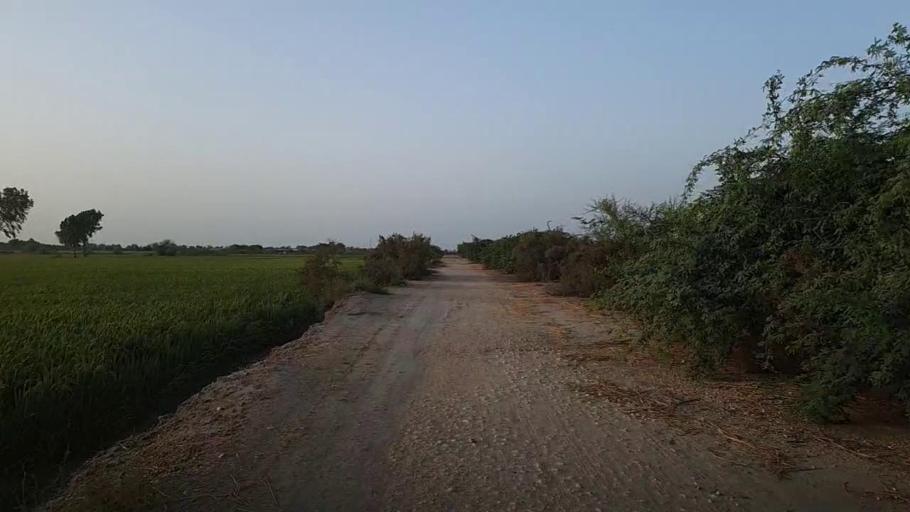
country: PK
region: Sindh
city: Kario
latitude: 24.7247
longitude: 68.4610
